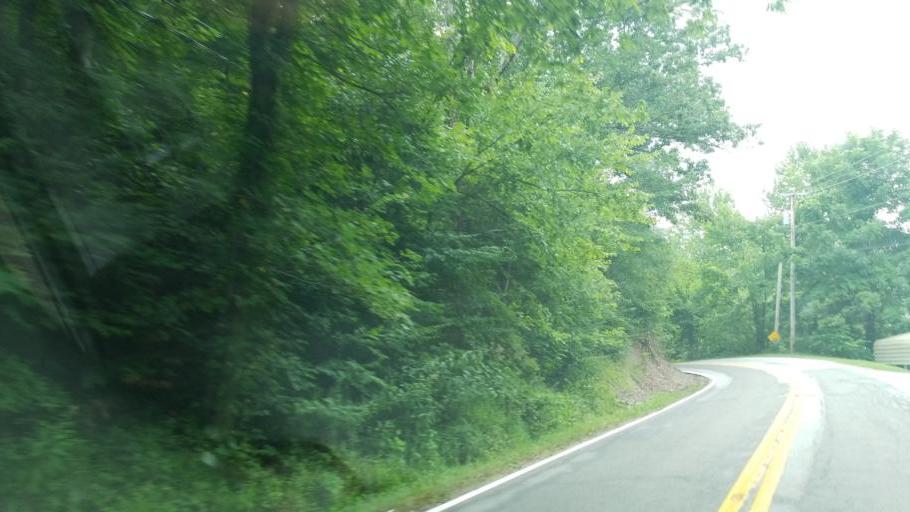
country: US
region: West Virginia
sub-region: Kanawha County
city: Alum Creek
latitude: 38.2858
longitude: -81.7793
